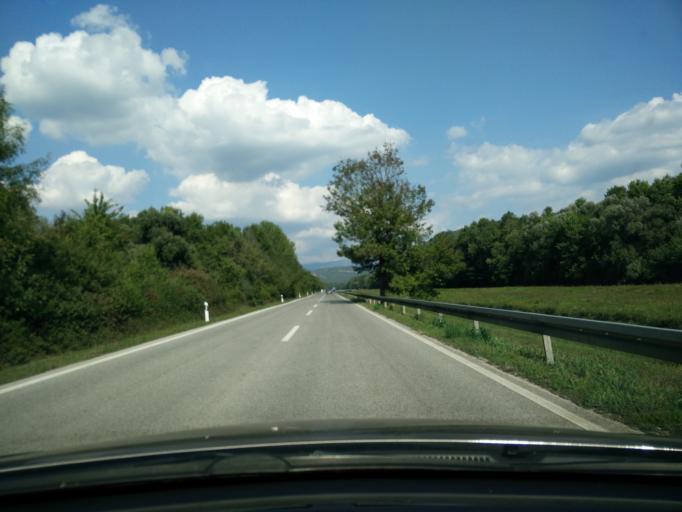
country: HR
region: Istarska
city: Karojba
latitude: 45.3524
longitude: 13.8501
